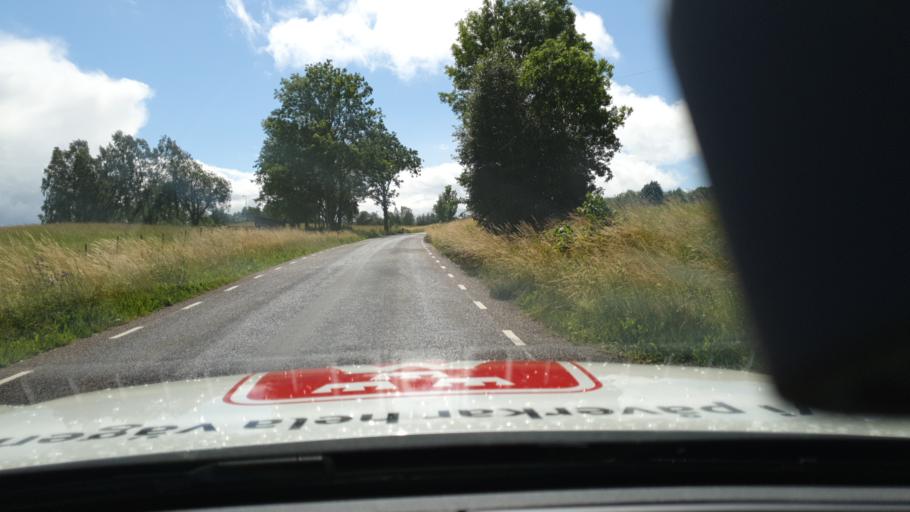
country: SE
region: Vaestra Goetaland
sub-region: Falkopings Kommun
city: Akarp
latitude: 58.1791
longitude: 13.6456
